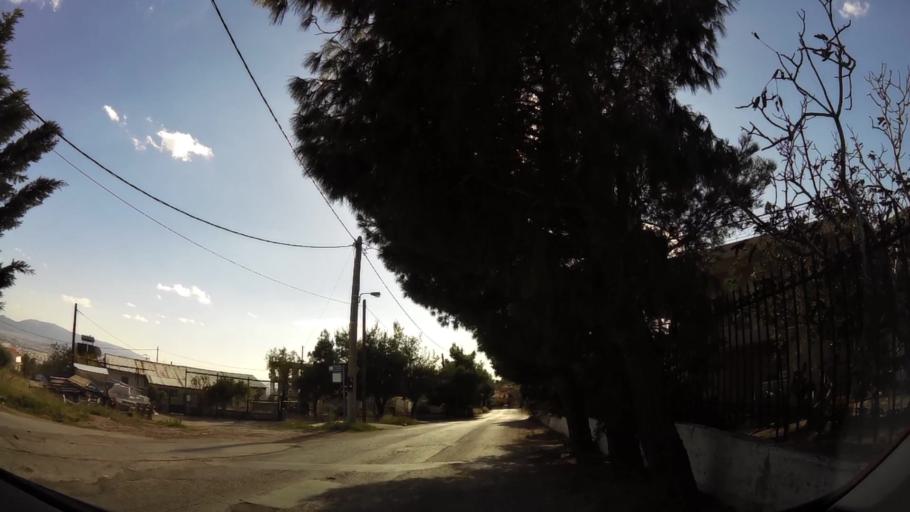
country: GR
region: Attica
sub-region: Nomarchia Anatolikis Attikis
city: Acharnes
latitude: 38.1149
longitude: 23.7239
